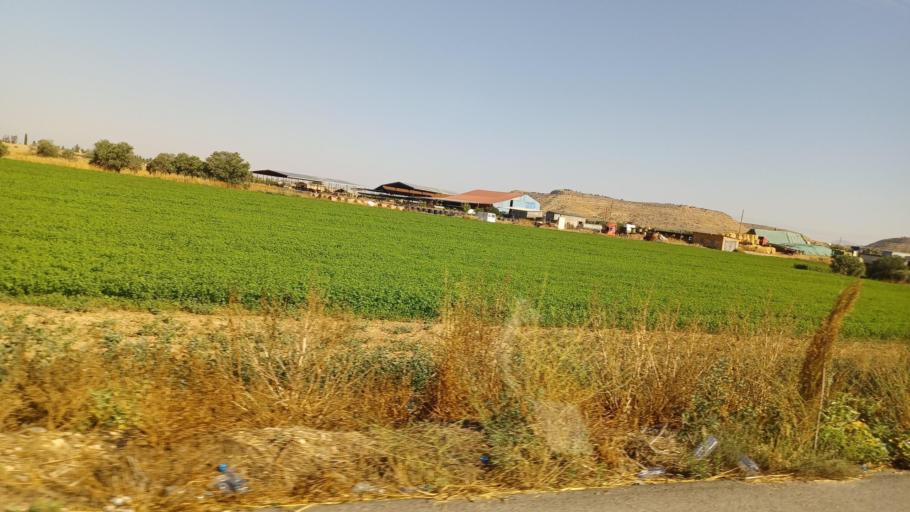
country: CY
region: Larnaka
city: Athienou
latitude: 35.0618
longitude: 33.5185
